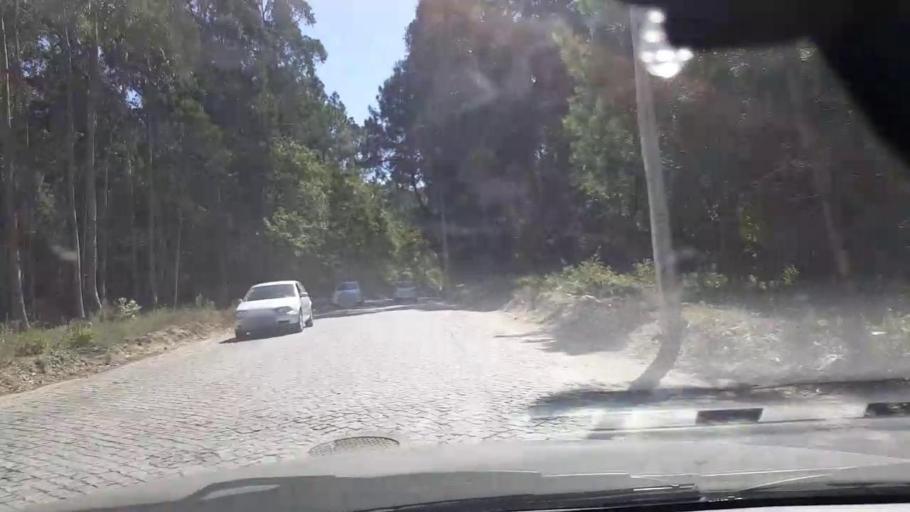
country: PT
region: Porto
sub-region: Vila do Conde
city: Arvore
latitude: 41.3282
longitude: -8.7280
